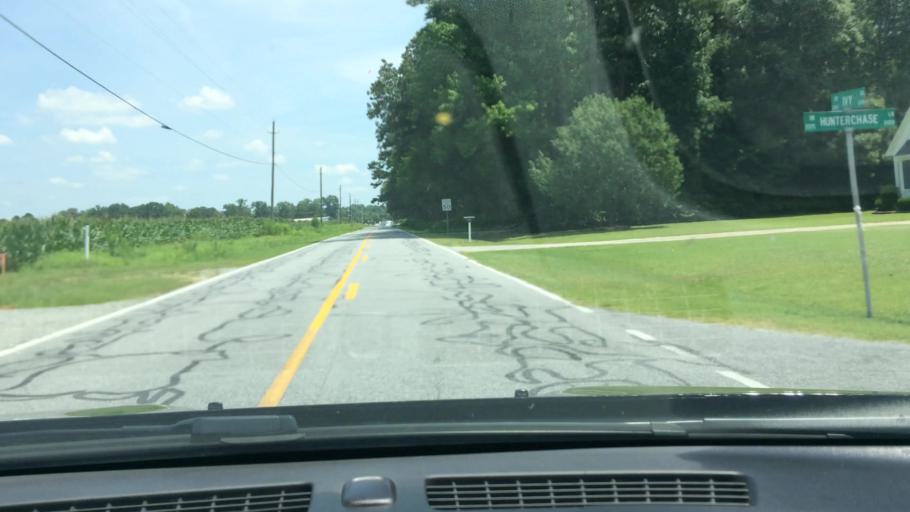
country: US
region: North Carolina
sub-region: Pitt County
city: Windsor
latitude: 35.5098
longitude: -77.3222
